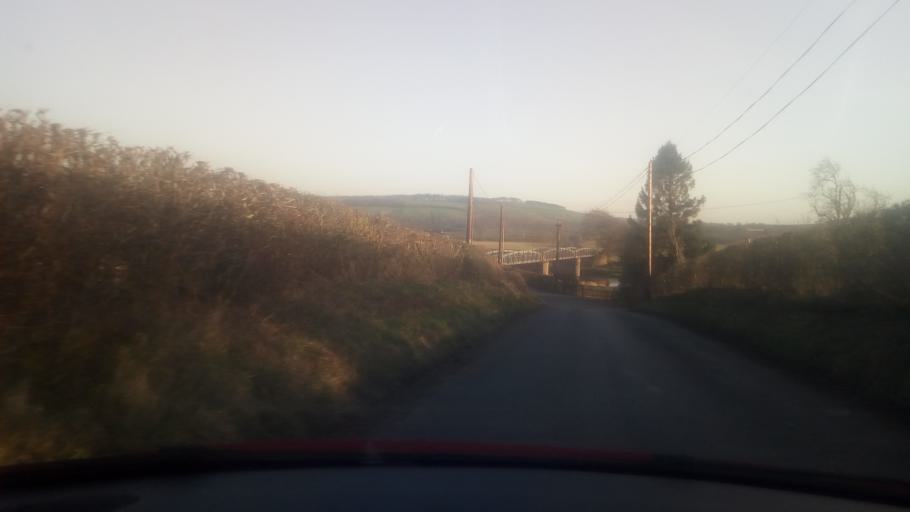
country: GB
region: Scotland
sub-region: The Scottish Borders
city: Jedburgh
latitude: 55.5227
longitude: -2.5182
